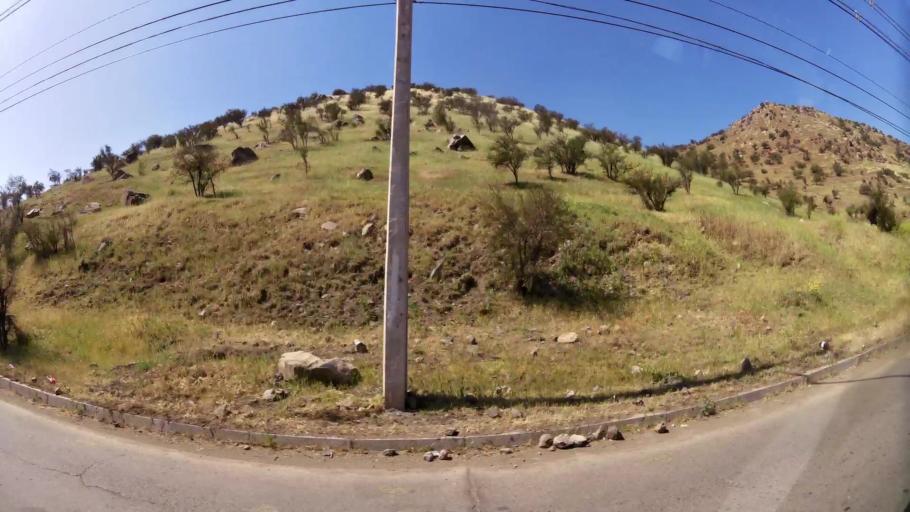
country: CL
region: Santiago Metropolitan
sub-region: Provincia de Santiago
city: Lo Prado
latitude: -33.3789
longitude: -70.7398
